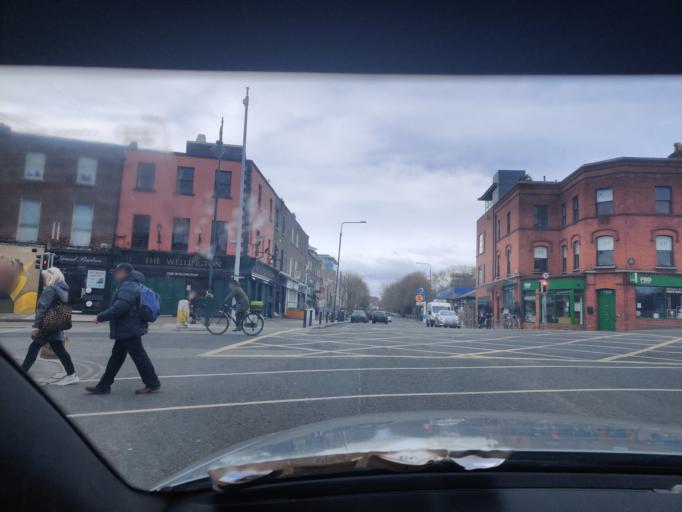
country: IE
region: Leinster
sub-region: Dublin City
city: Dublin
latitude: 53.3341
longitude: -6.2449
